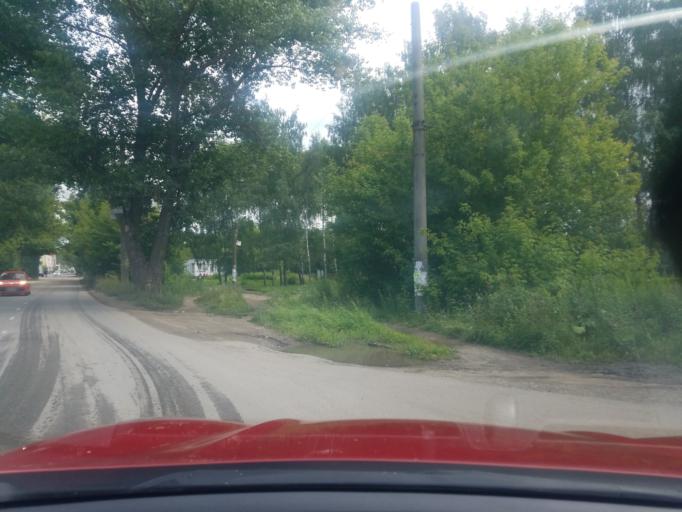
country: RU
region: Orjol
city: Znamenka
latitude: 52.9184
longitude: 35.9867
